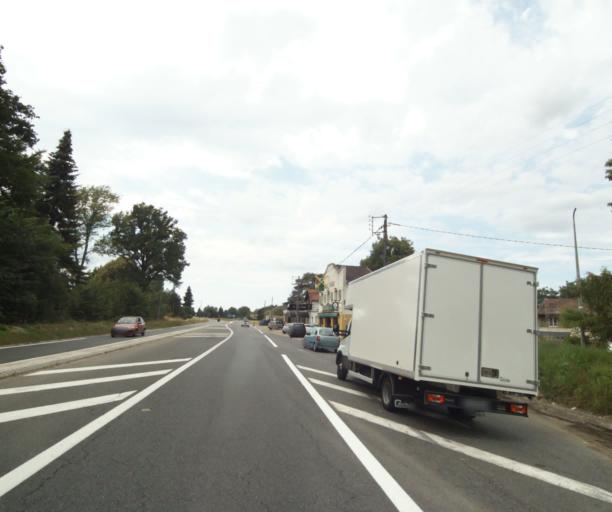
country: FR
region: Ile-de-France
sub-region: Departement de Seine-et-Marne
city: Chailly-en-Biere
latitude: 48.4524
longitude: 2.6227
